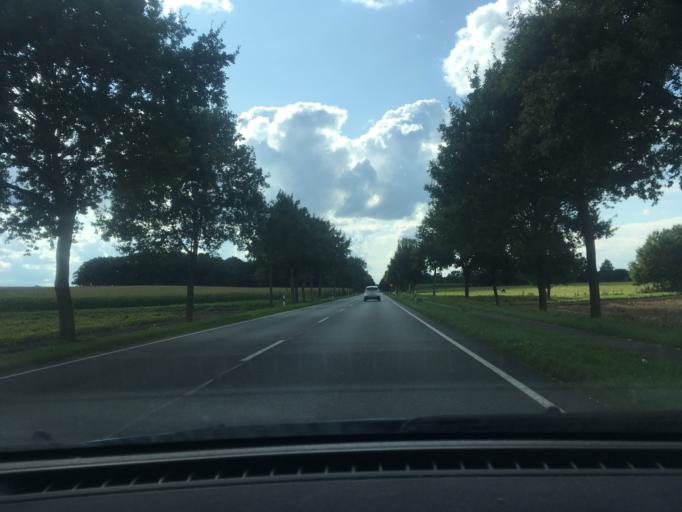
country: DE
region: Lower Saxony
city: Soltau
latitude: 52.9901
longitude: 9.9015
